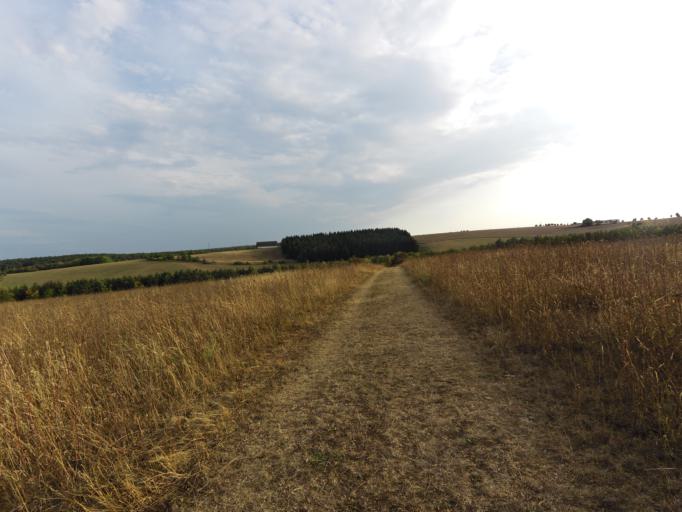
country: DE
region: Bavaria
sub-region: Regierungsbezirk Unterfranken
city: Zell am Main
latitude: 49.8046
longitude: 9.8618
